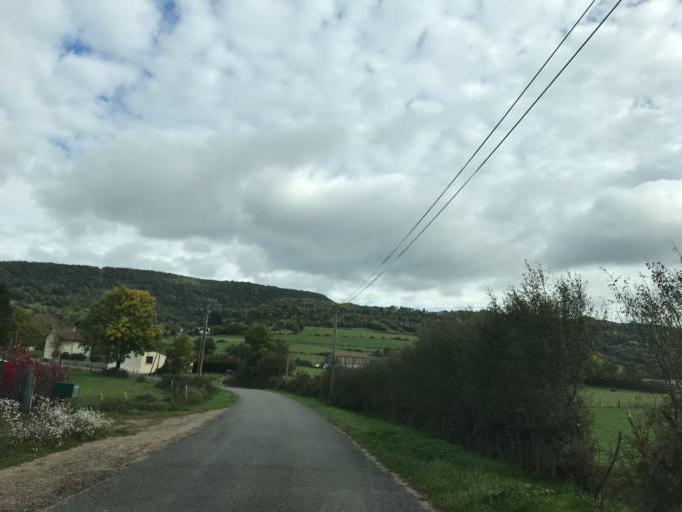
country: FR
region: Rhone-Alpes
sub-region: Departement de l'Ain
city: Cuisiat
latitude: 46.3293
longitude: 5.4397
